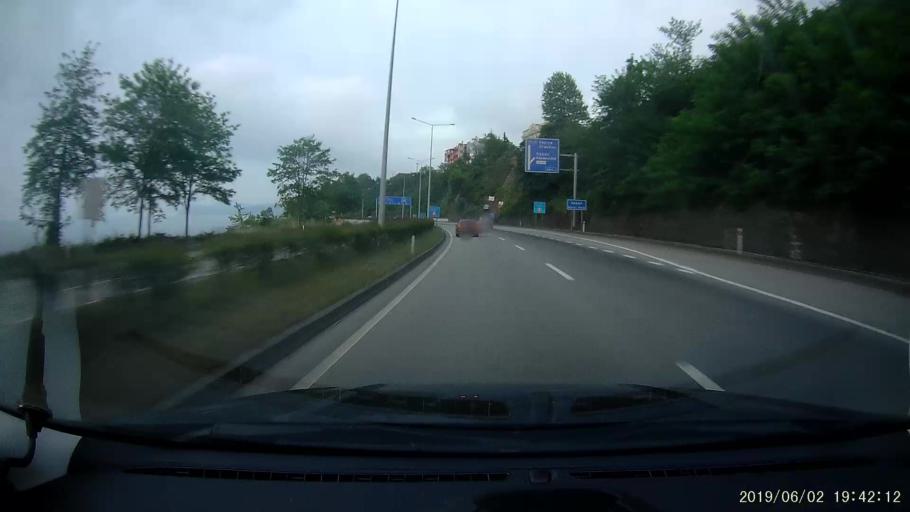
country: TR
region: Giresun
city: Kesap
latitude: 40.9154
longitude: 38.4984
